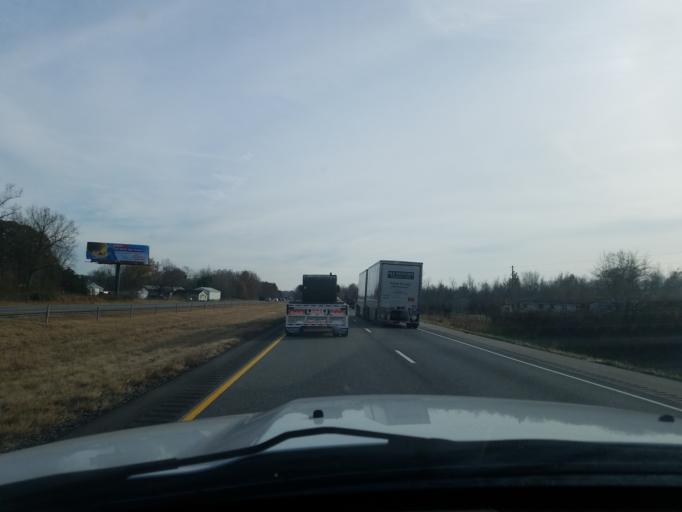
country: US
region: Indiana
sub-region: Jackson County
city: Seymour
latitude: 38.9206
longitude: -85.8363
